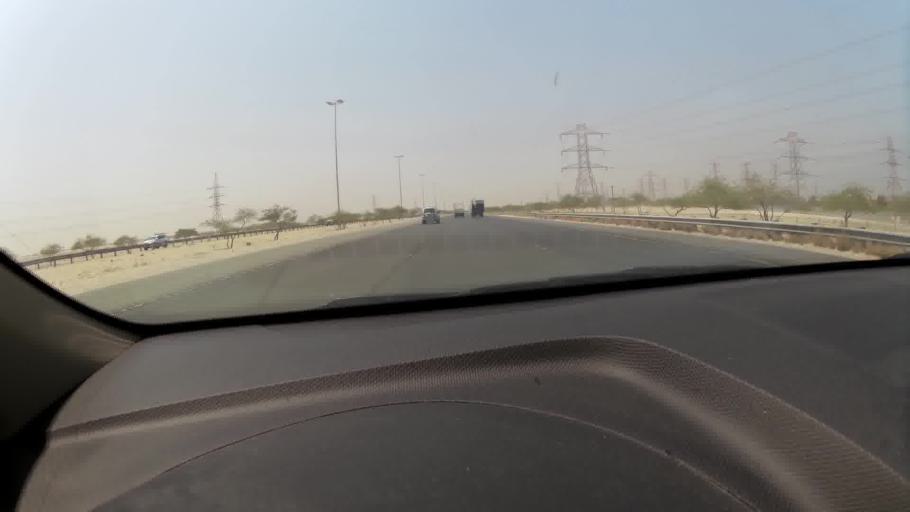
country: KW
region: Al Ahmadi
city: Al Fahahil
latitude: 28.9434
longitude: 48.1433
